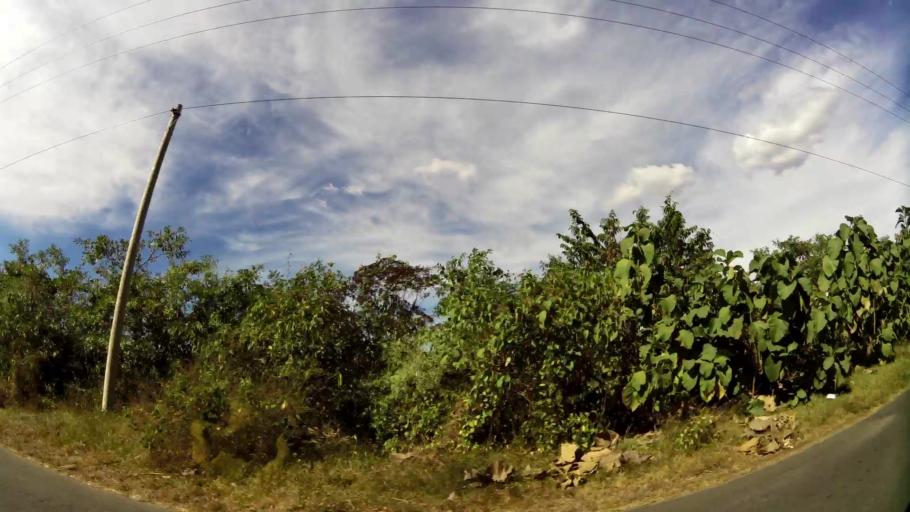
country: SV
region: San Salvador
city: Aguilares
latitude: 13.9633
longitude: -89.1229
